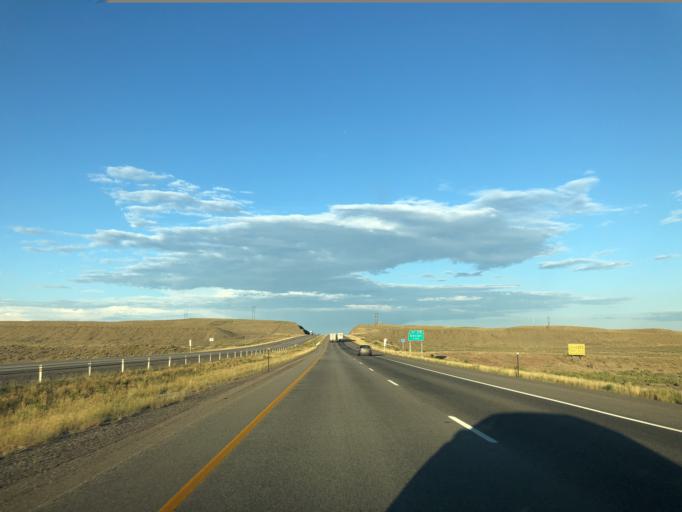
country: US
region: Wyoming
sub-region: Carbon County
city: Rawlins
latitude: 41.7833
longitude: -107.1566
